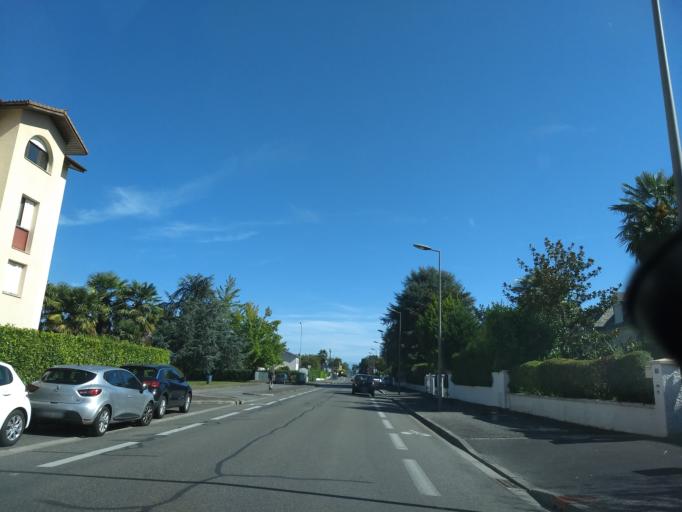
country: FR
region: Aquitaine
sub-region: Departement des Pyrenees-Atlantiques
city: Idron
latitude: 43.3097
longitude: -0.3314
